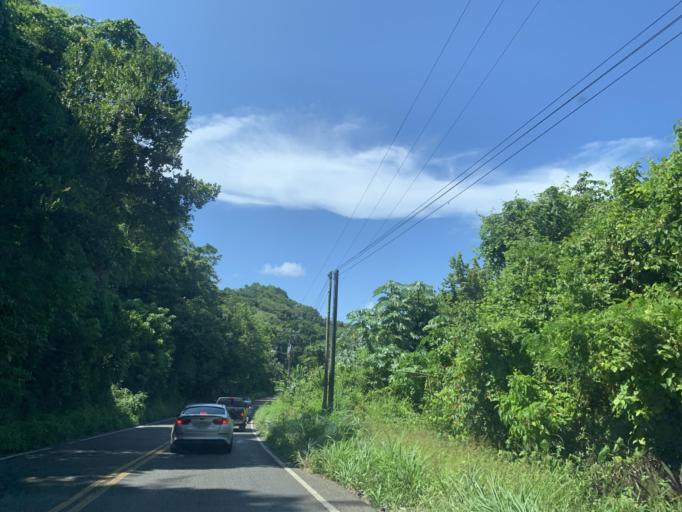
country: DO
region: Maria Trinidad Sanchez
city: Cabrera
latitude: 19.6563
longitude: -69.9362
